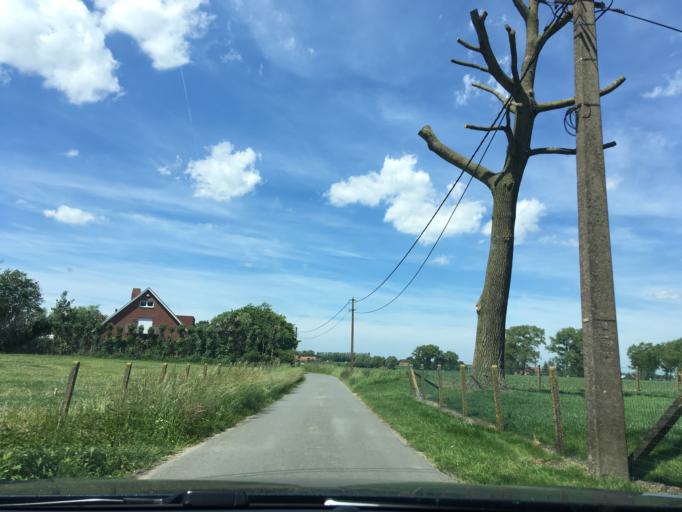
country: BE
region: Flanders
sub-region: Provincie West-Vlaanderen
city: Lichtervelde
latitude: 51.0234
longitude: 3.1777
